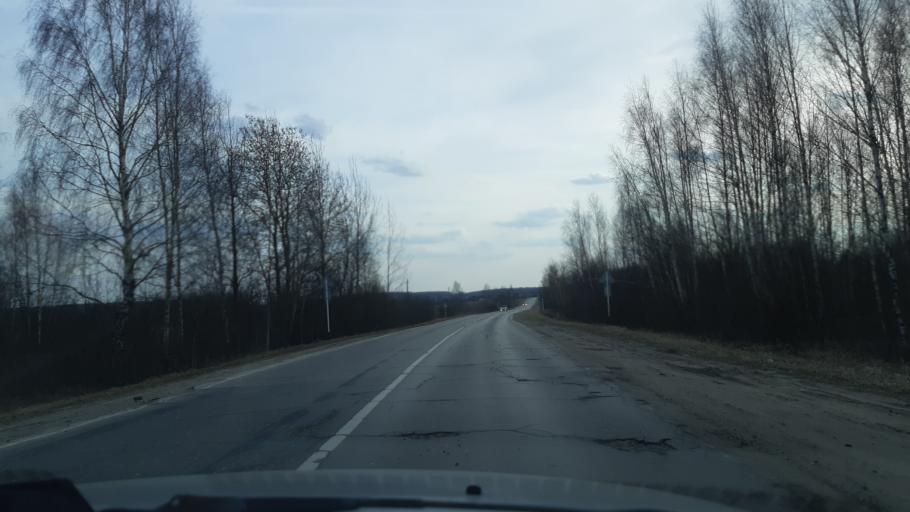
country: RU
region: Vladimir
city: Luknovo
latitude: 56.2213
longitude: 42.0340
